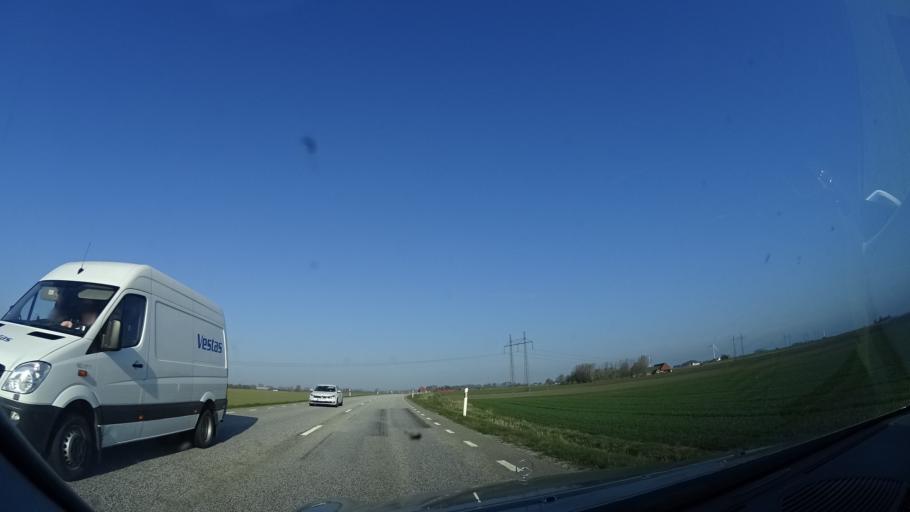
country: SE
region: Skane
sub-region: Svalovs Kommun
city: Teckomatorp
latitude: 55.8767
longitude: 13.0529
